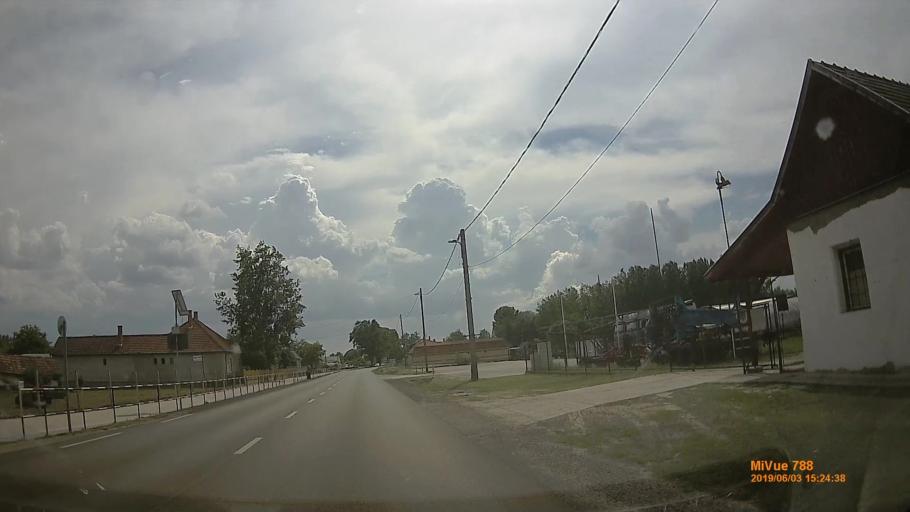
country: HU
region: Bacs-Kiskun
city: Tazlar
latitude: 46.6145
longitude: 19.4754
